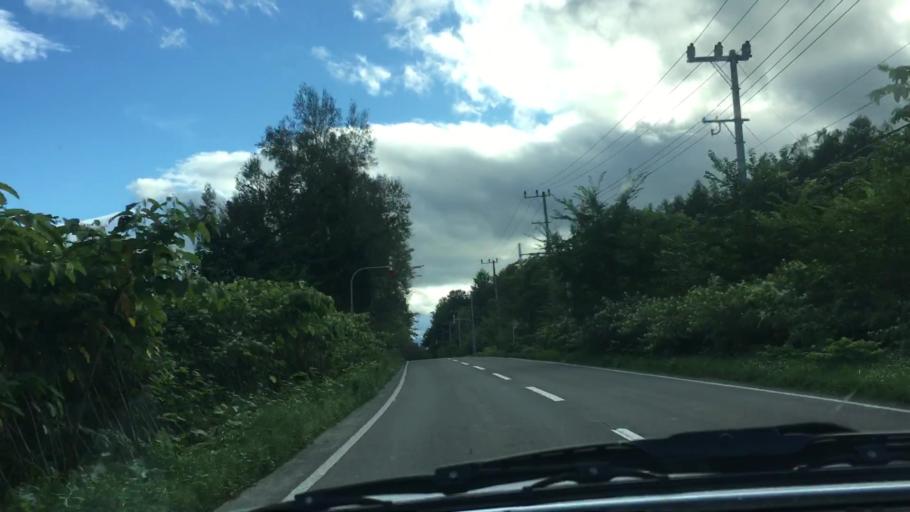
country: JP
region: Hokkaido
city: Otofuke
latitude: 43.1710
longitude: 142.9136
